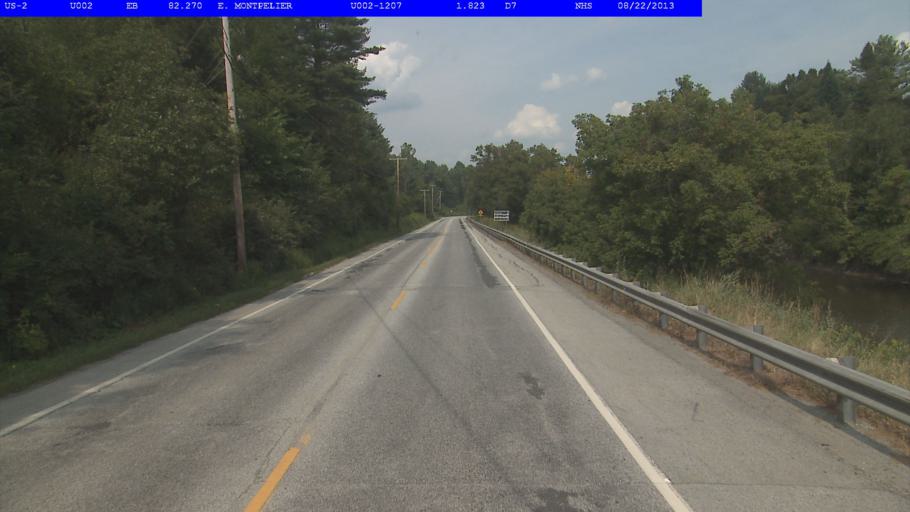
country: US
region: Vermont
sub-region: Washington County
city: Barre
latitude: 44.2593
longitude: -72.5009
